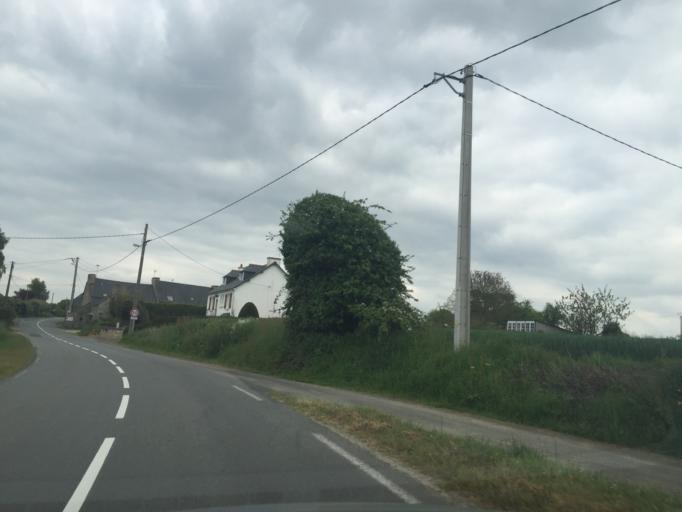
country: FR
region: Brittany
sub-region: Departement des Cotes-d'Armor
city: Saint-Cast-le-Guildo
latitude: 48.6042
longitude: -2.2536
